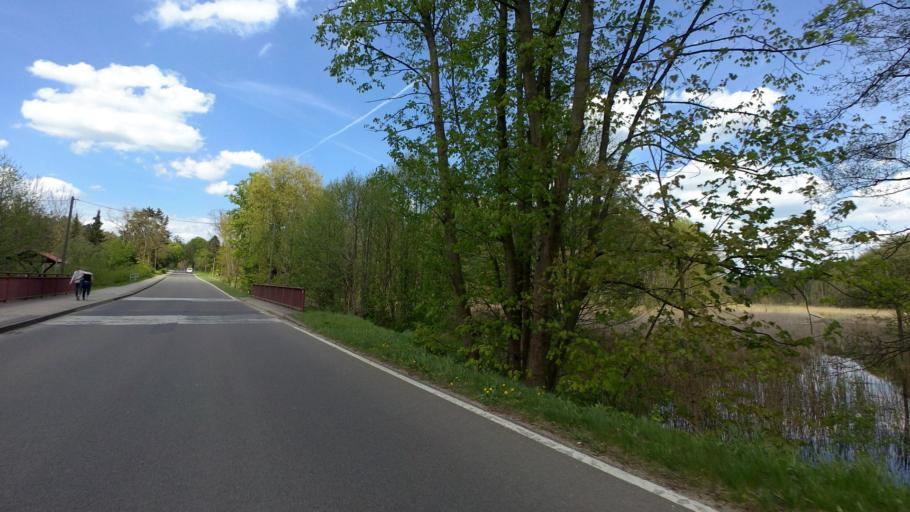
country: DE
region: Brandenburg
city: Milmersdorf
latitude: 53.0744
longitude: 13.6229
